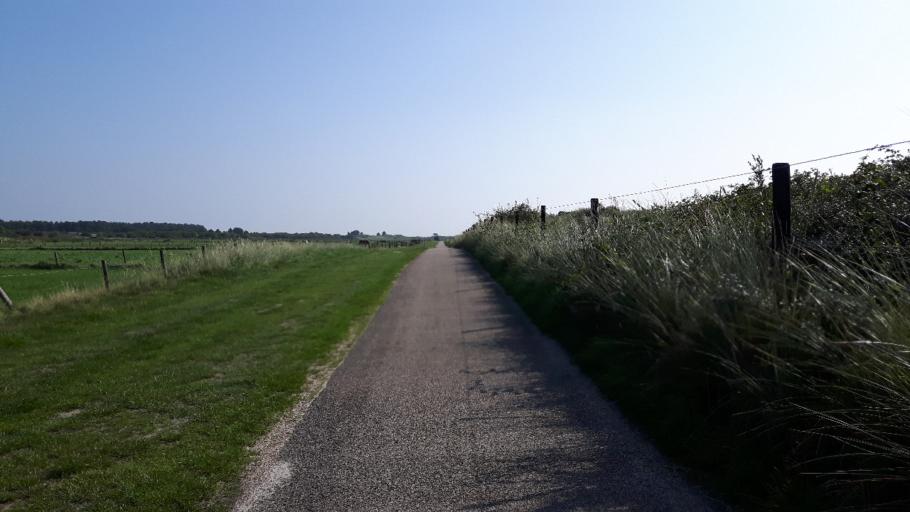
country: NL
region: Friesland
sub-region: Gemeente Ameland
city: Nes
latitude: 53.4554
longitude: 5.8086
